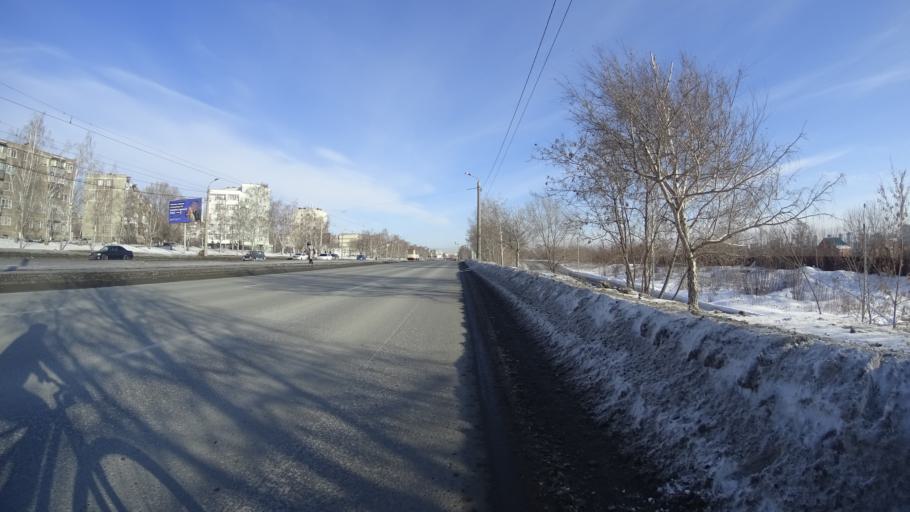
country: RU
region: Chelyabinsk
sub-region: Gorod Chelyabinsk
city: Chelyabinsk
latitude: 55.1889
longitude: 61.3446
